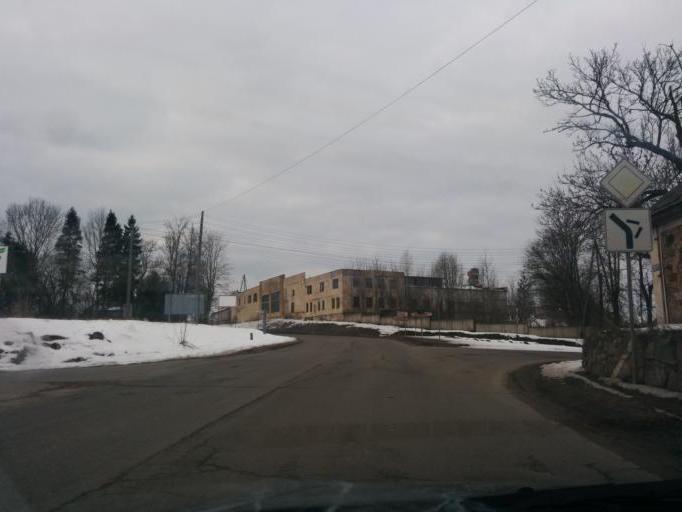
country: LV
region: Gulbenes Rajons
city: Gulbene
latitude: 57.1837
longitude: 26.7370
